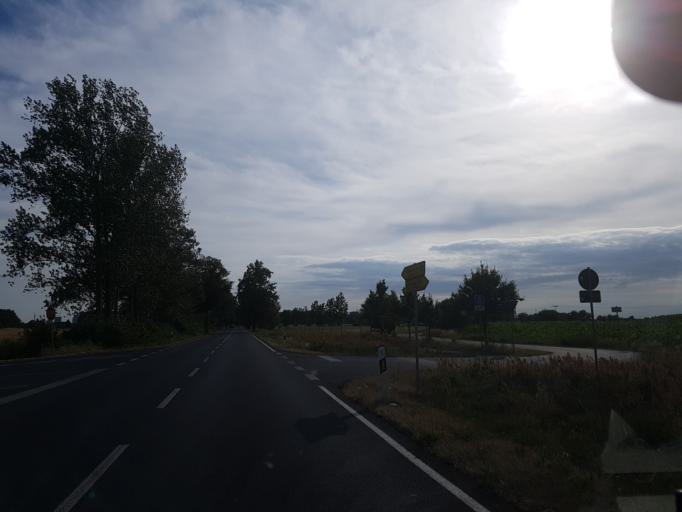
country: DE
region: Brandenburg
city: Herzberg
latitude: 51.7188
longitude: 13.2874
